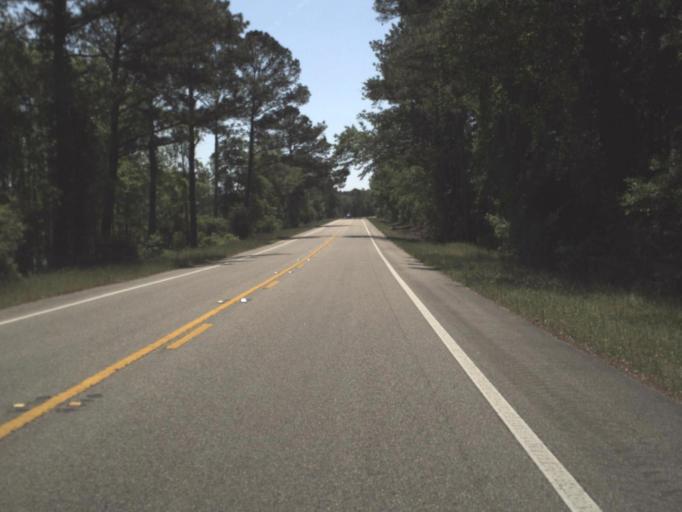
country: US
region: Florida
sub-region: Jackson County
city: Marianna
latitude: 30.6359
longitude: -85.1911
